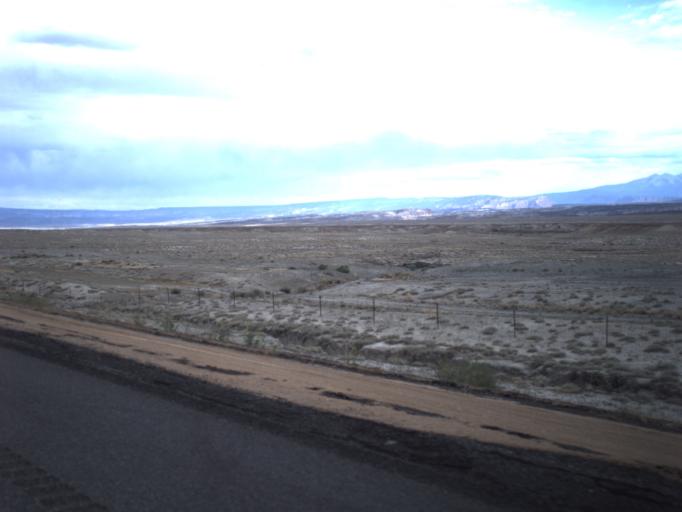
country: US
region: Utah
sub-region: Grand County
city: Moab
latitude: 38.9352
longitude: -109.4675
